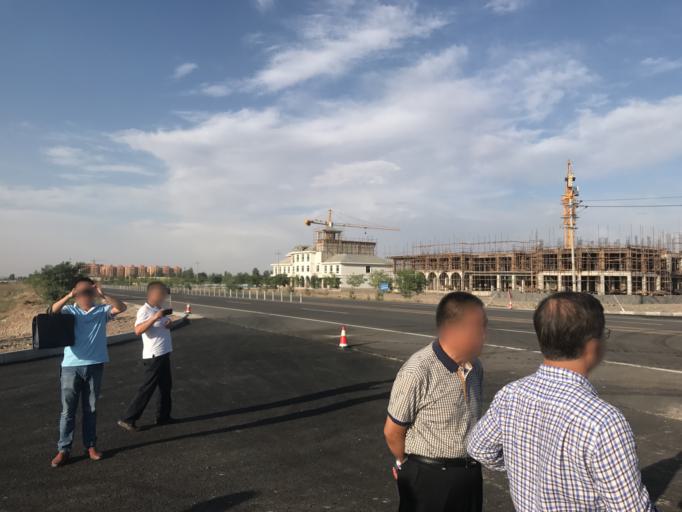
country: CN
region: Gansu Sheng
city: Gulang
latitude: 37.6539
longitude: 103.0114
